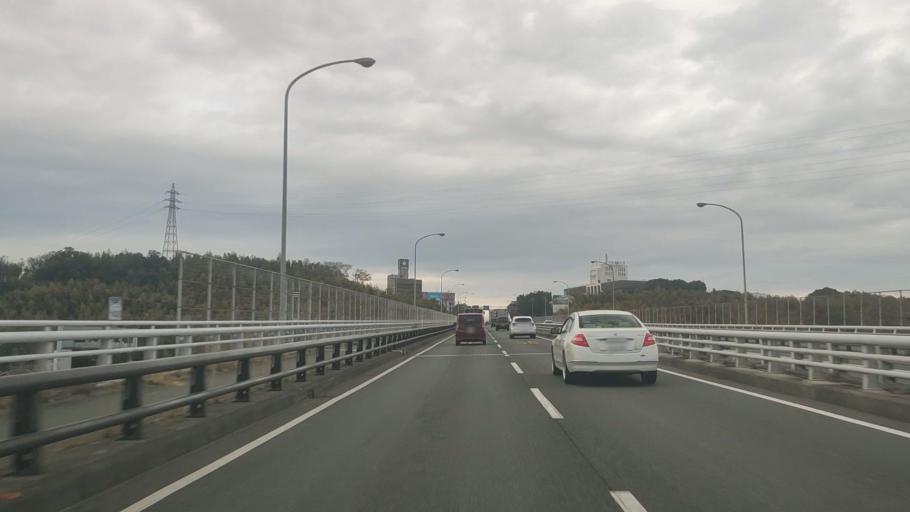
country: JP
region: Kumamoto
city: Ozu
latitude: 32.8479
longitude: 130.7820
